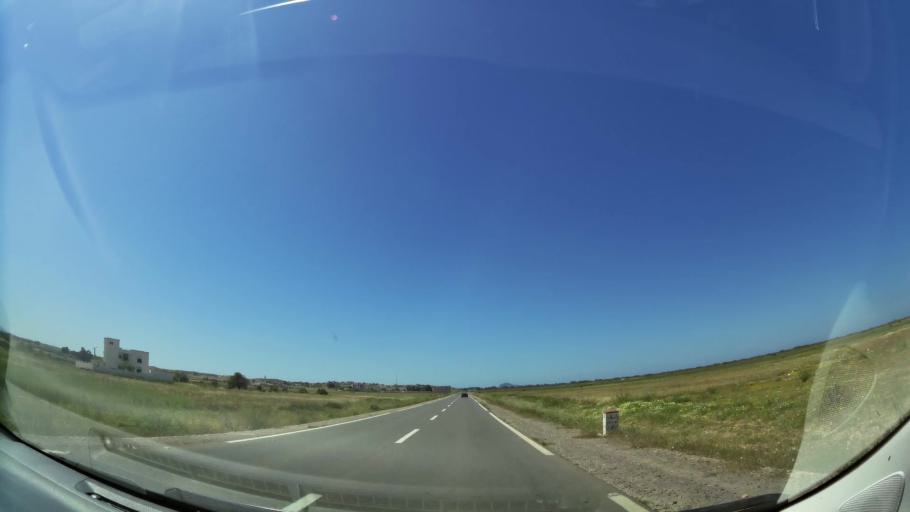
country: MA
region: Oriental
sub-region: Berkane-Taourirt
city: Madagh
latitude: 35.1148
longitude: -2.3665
